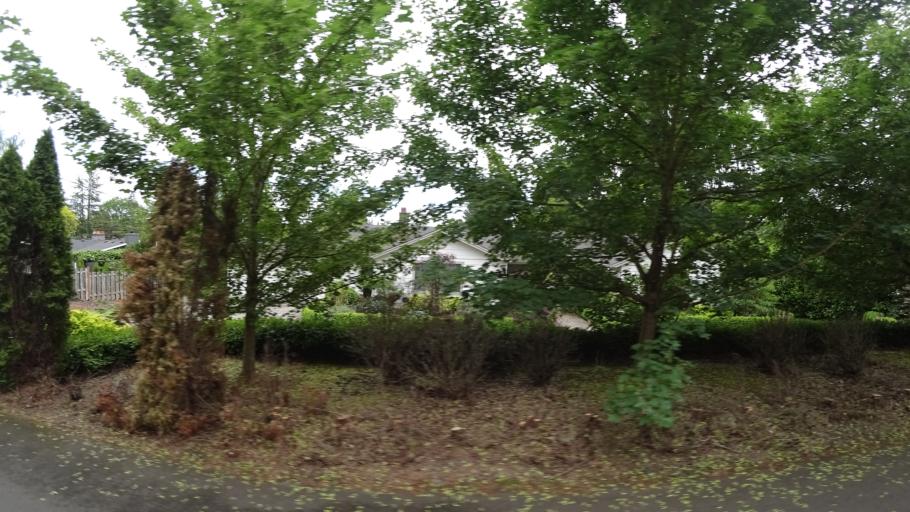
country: US
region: Oregon
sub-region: Washington County
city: Raleigh Hills
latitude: 45.4799
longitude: -122.7599
